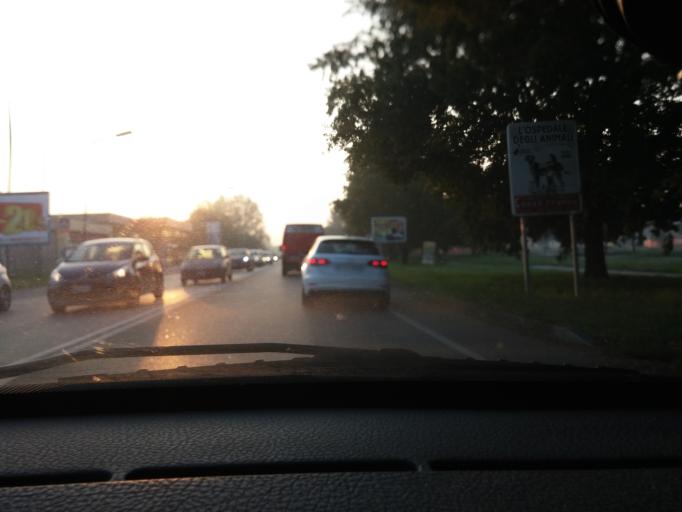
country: IT
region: Emilia-Romagna
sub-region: Provincia di Ferrara
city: Ferrara
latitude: 44.8182
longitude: 11.6053
